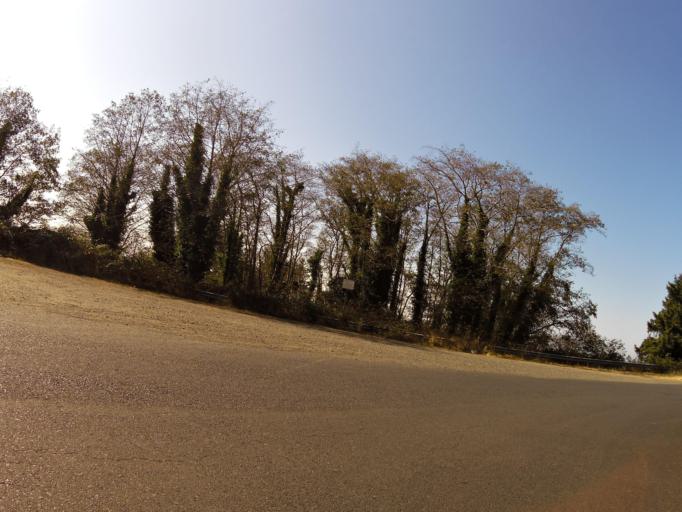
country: US
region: Oregon
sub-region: Tillamook County
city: Pacific City
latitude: 45.1412
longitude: -123.9694
